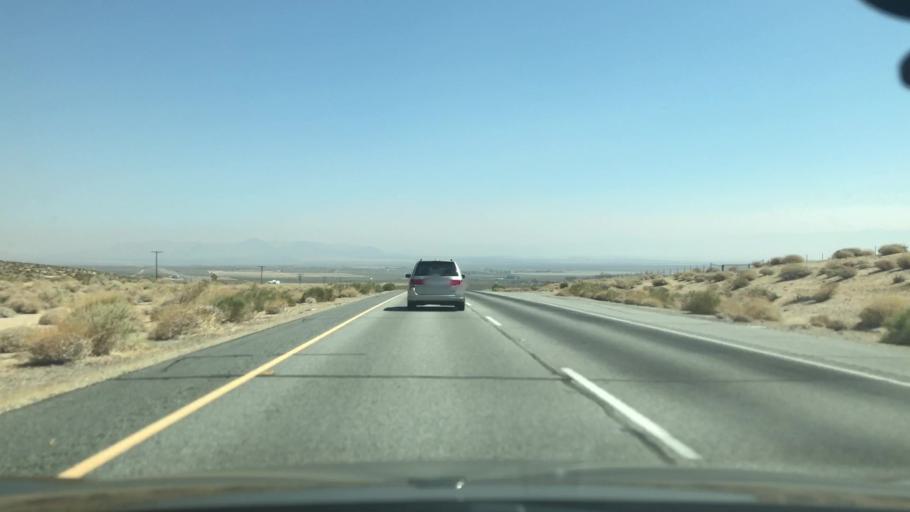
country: US
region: California
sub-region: Kern County
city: Inyokern
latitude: 35.6730
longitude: -117.8696
